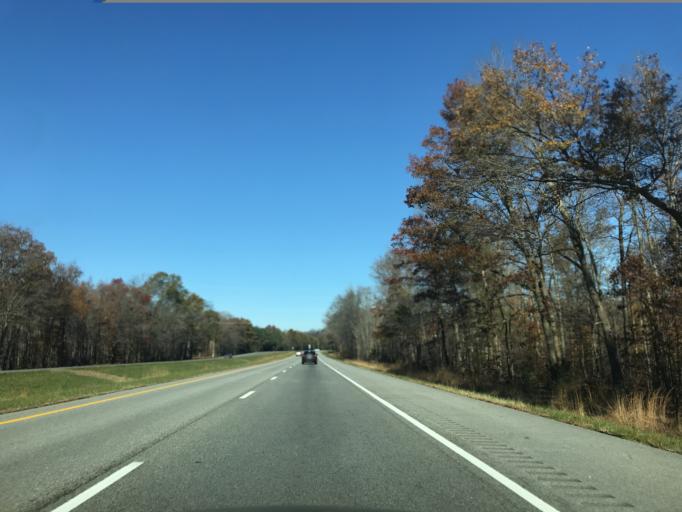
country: US
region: Maryland
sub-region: Queen Anne's County
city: Kingstown
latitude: 39.2328
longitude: -75.8749
